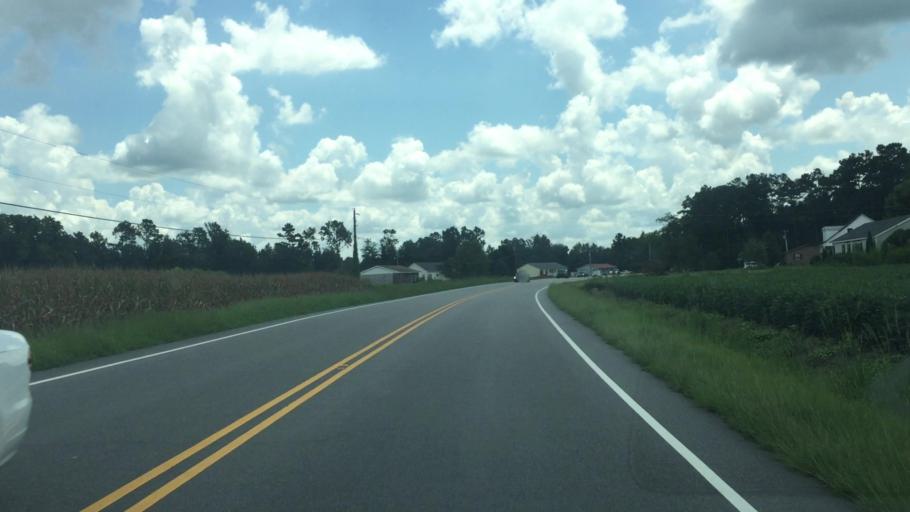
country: US
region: North Carolina
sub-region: Columbus County
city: Chadbourn
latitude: 34.2763
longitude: -78.8138
